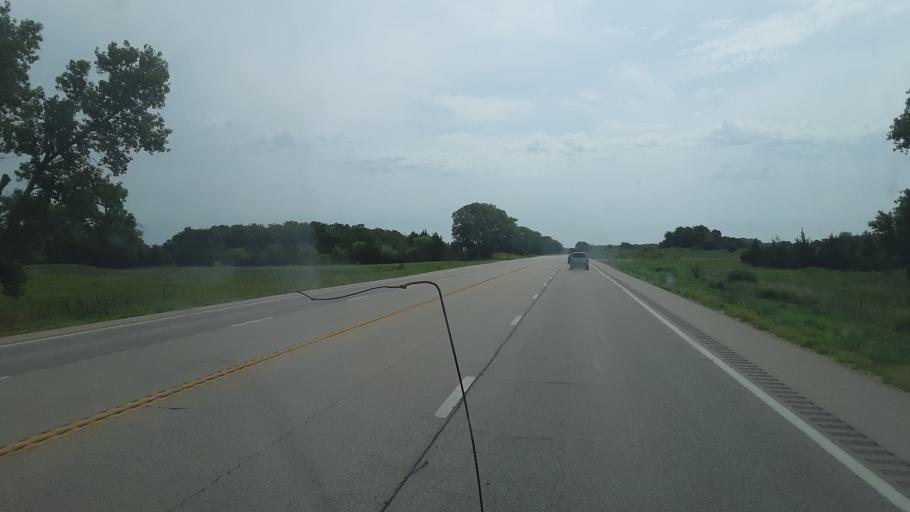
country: US
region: Kansas
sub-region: Rice County
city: Sterling
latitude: 37.9846
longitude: -98.2908
